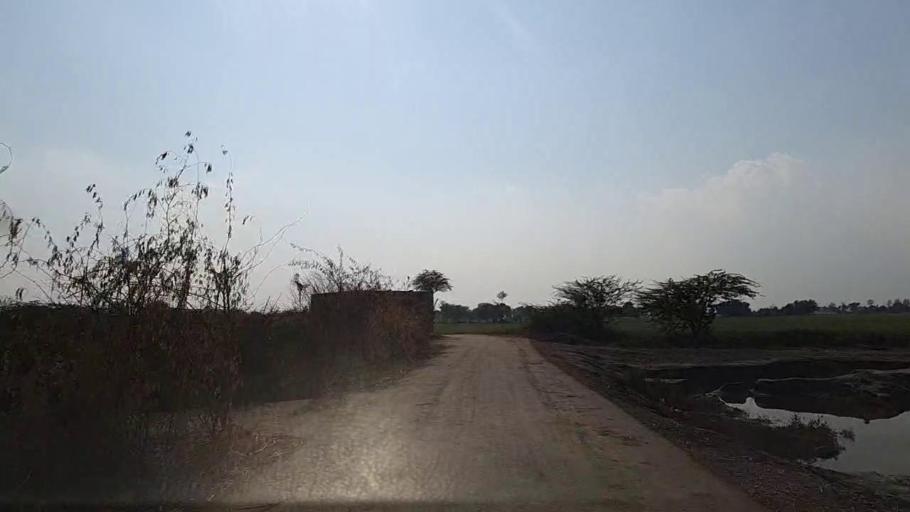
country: PK
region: Sindh
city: Jam Sahib
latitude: 26.2782
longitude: 68.6116
